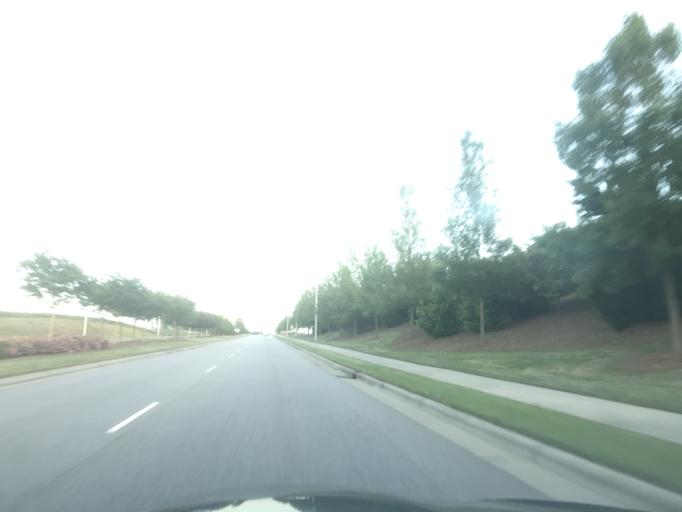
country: US
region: North Carolina
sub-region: Wake County
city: Knightdale
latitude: 35.7734
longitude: -78.4306
